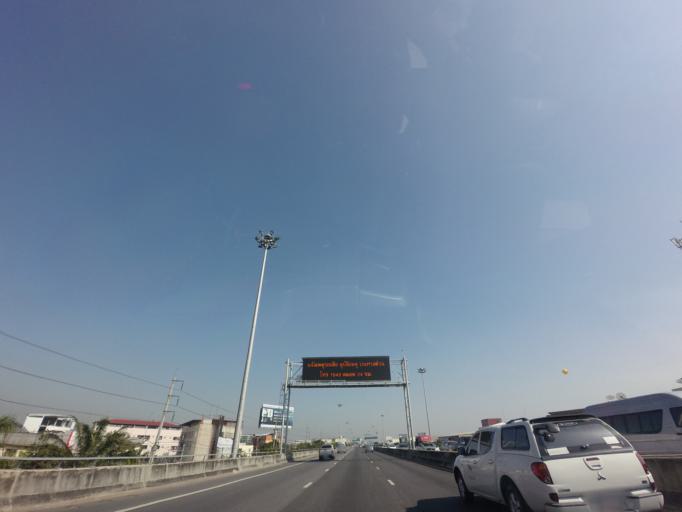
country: TH
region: Bangkok
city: Lat Phrao
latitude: 13.8025
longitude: 100.6159
